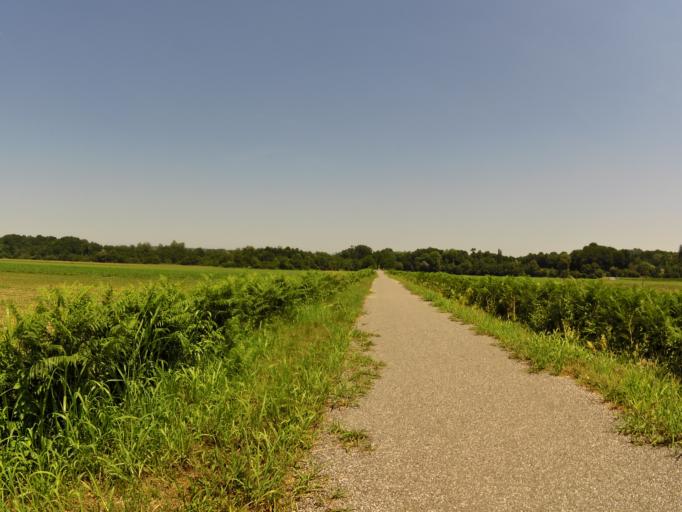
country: FR
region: Aquitaine
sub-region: Departement des Pyrenees-Atlantiques
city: Salies-de-Bearn
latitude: 43.4590
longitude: -0.9853
